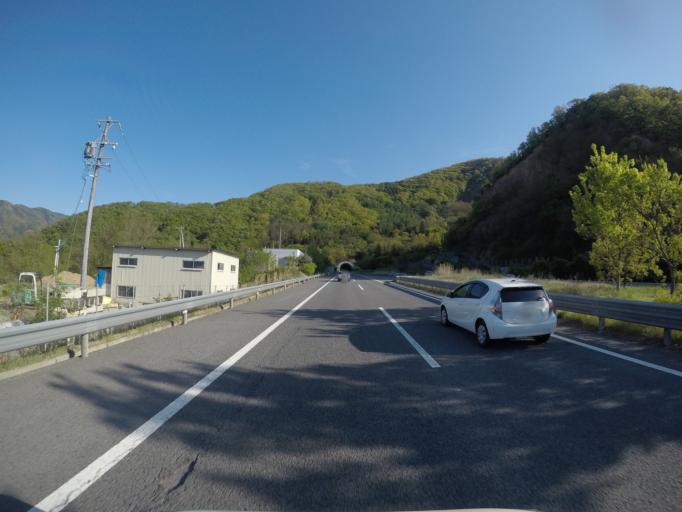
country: JP
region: Nagano
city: Nagano-shi
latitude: 36.5327
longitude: 138.1406
